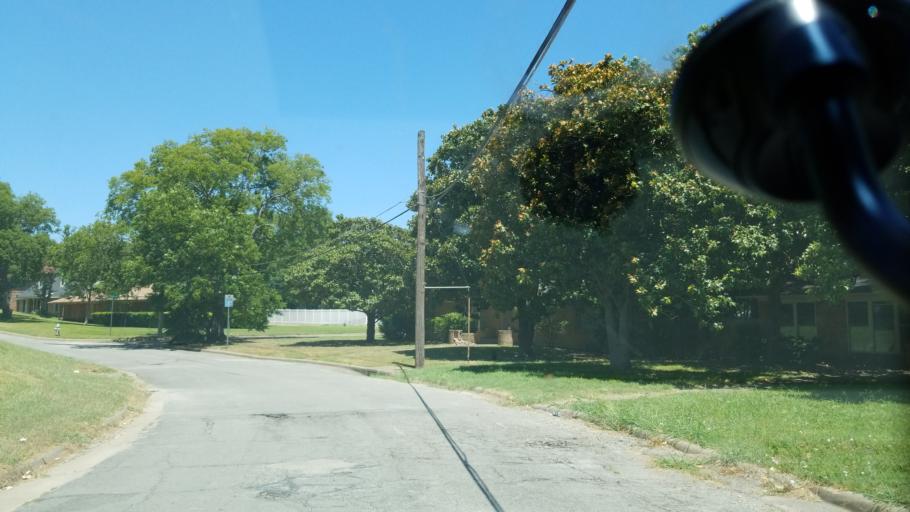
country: US
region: Texas
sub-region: Dallas County
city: Cockrell Hill
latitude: 32.6908
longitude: -96.8320
